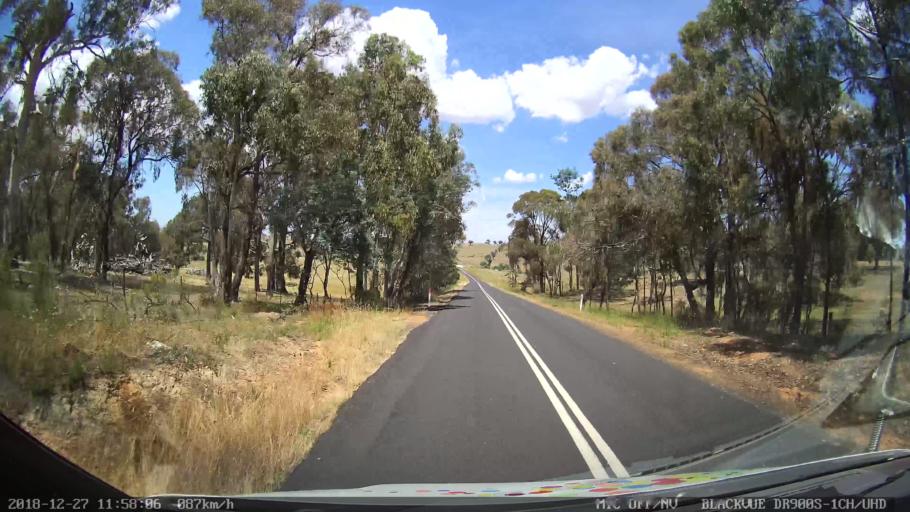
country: AU
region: New South Wales
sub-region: Blayney
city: Blayney
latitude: -33.7198
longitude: 149.3864
